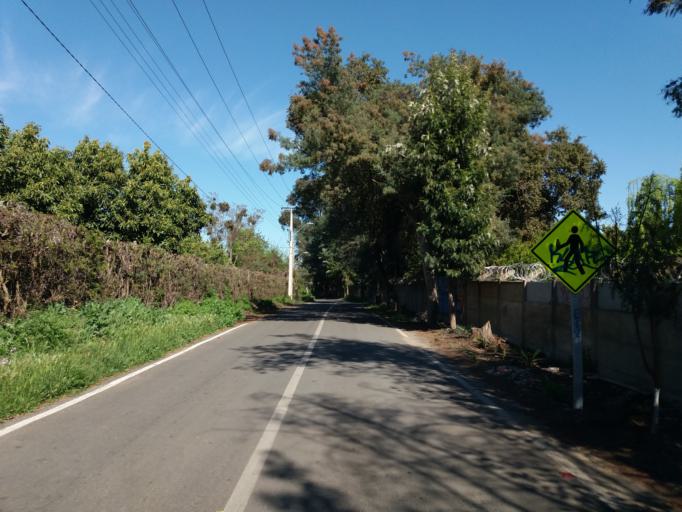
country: CL
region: Valparaiso
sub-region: Provincia de Marga Marga
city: Limache
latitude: -33.0000
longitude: -71.1804
